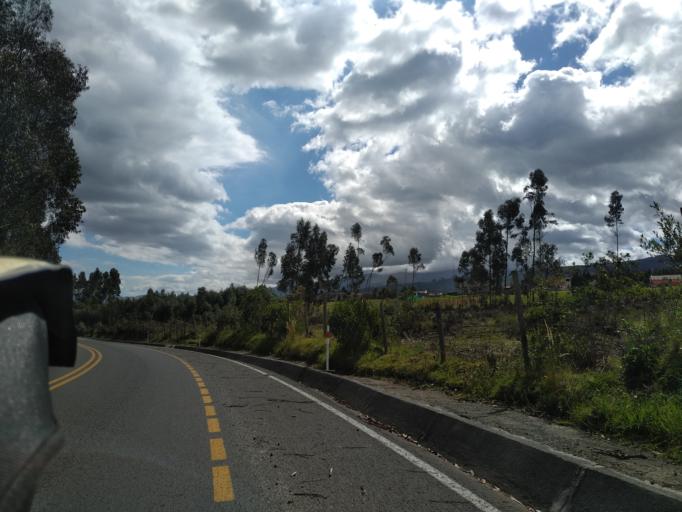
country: EC
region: Cotopaxi
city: Saquisili
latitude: -0.7009
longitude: -78.5789
